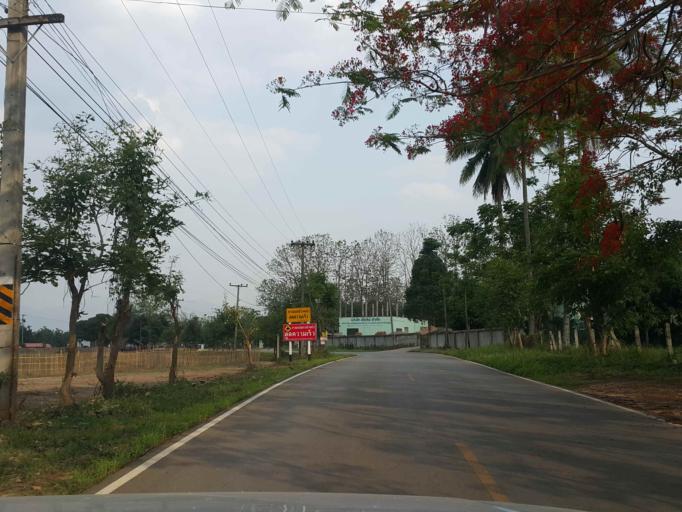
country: TH
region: Chiang Mai
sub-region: Amphoe Chiang Dao
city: Chiang Dao
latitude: 19.3789
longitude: 98.9440
